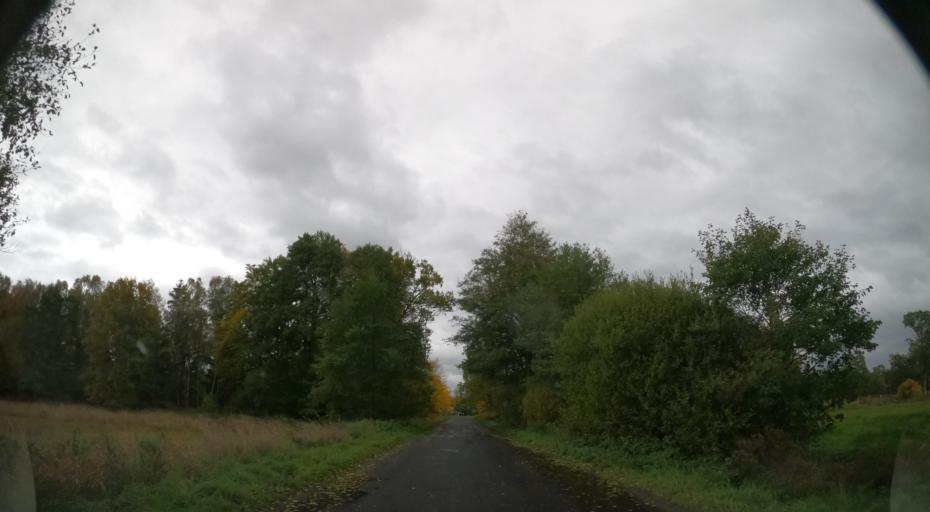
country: PL
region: West Pomeranian Voivodeship
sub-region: Powiat goleniowski
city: Stepnica
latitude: 53.6589
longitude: 14.6609
